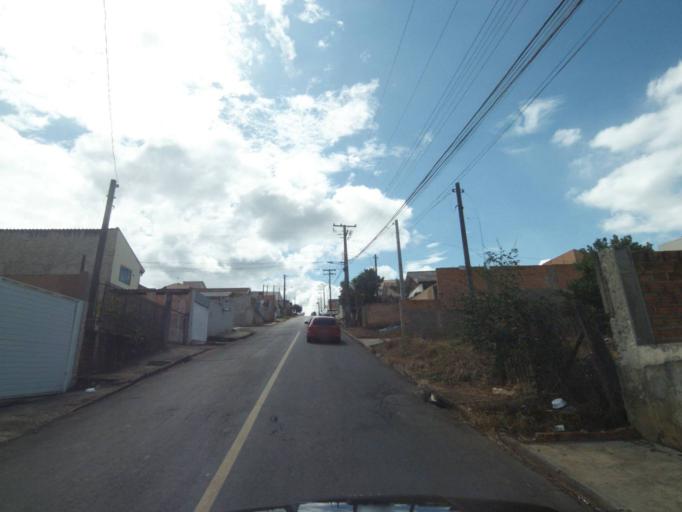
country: BR
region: Parana
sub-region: Telemaco Borba
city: Telemaco Borba
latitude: -24.3179
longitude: -50.6311
